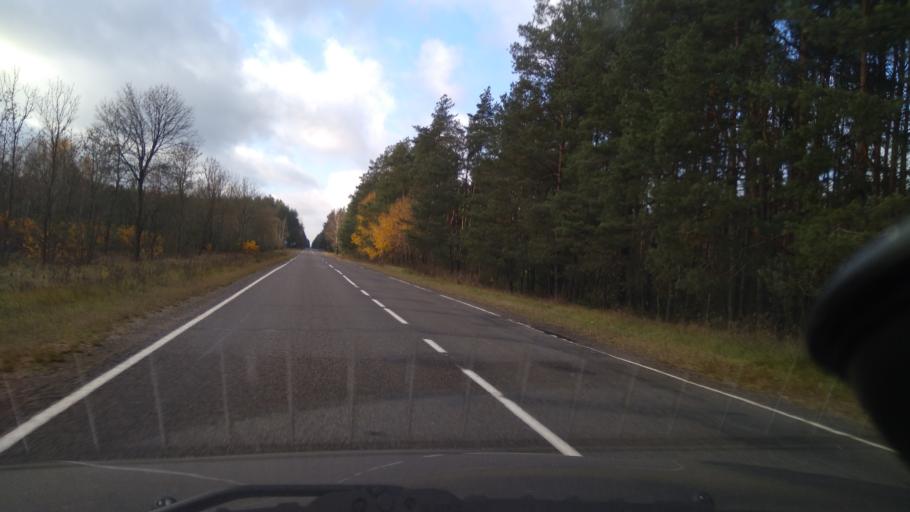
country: BY
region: Minsk
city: Slutsk
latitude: 53.2292
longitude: 27.7114
